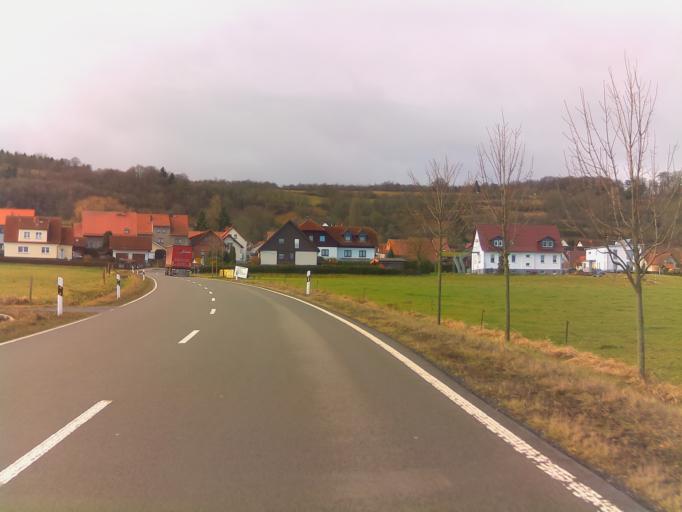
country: DE
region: Thuringia
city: Dermbach
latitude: 50.7238
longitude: 10.0998
